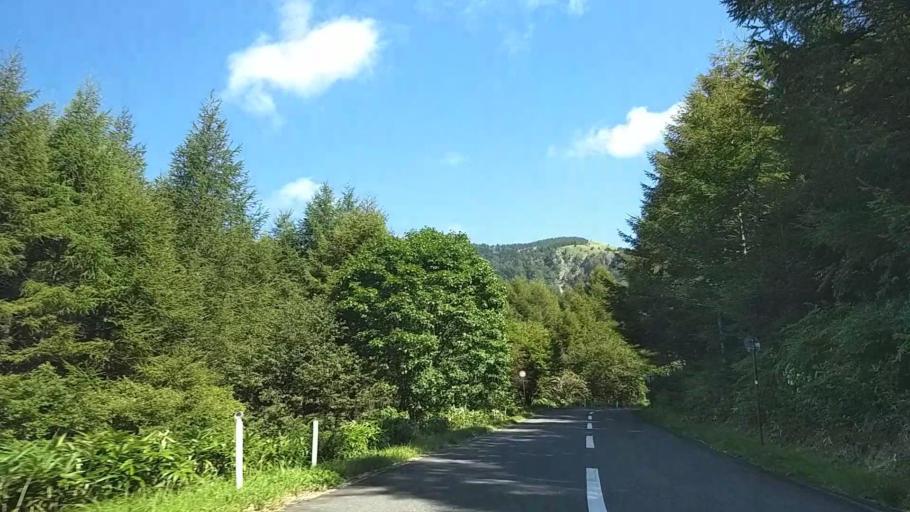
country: JP
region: Nagano
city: Suwa
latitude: 36.1902
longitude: 138.1220
